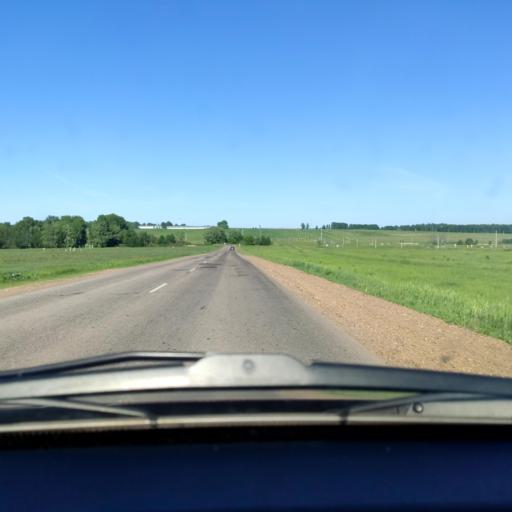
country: RU
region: Bashkortostan
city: Mikhaylovka
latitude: 54.8260
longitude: 55.7727
